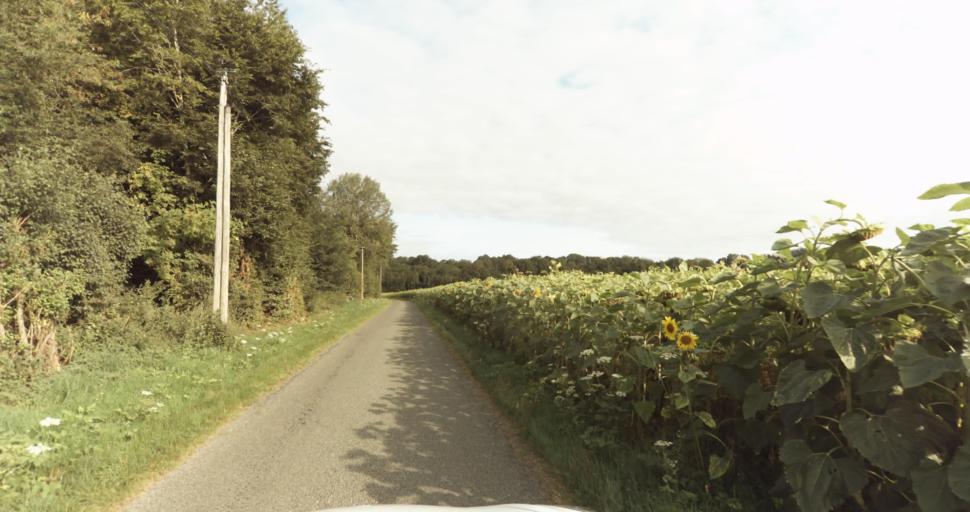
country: FR
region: Haute-Normandie
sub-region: Departement de l'Eure
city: Saint-Germain-sur-Avre
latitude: 48.8278
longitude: 1.2551
